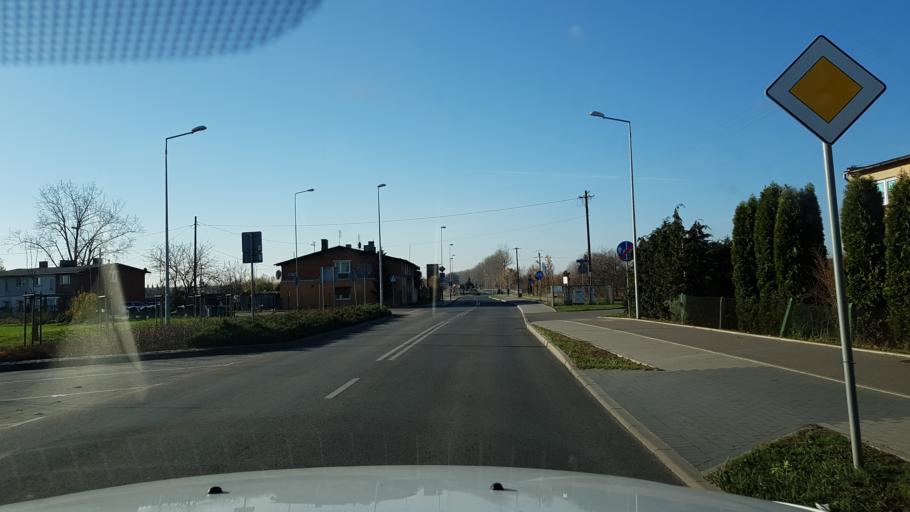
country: PL
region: West Pomeranian Voivodeship
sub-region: Powiat stargardzki
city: Stargard Szczecinski
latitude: 53.3274
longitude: 15.0154
